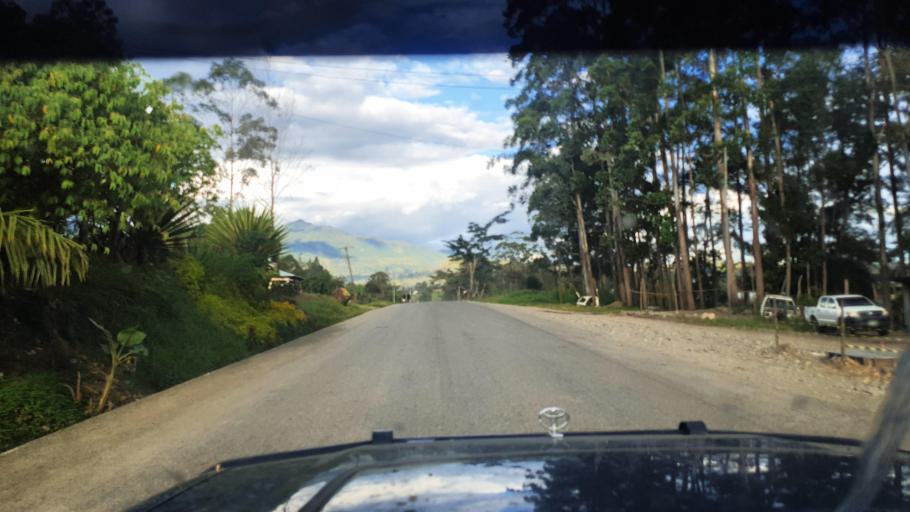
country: PG
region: Jiwaka
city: Minj
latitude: -5.9414
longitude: 144.8339
